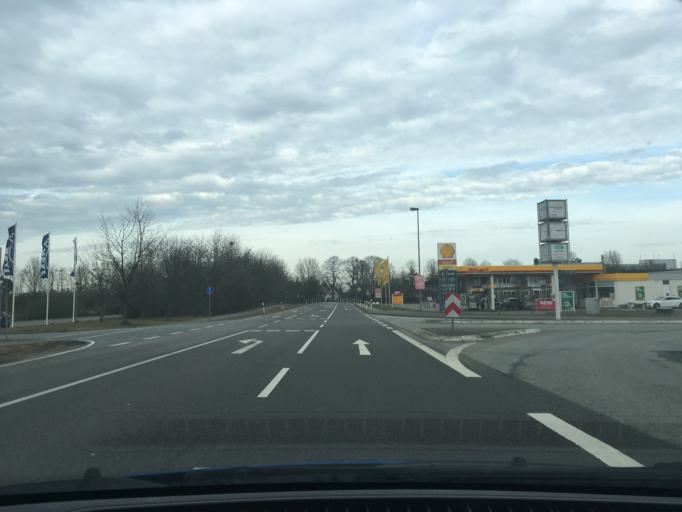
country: DE
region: Mecklenburg-Vorpommern
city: Zarrentin
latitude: 53.5451
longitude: 10.9078
